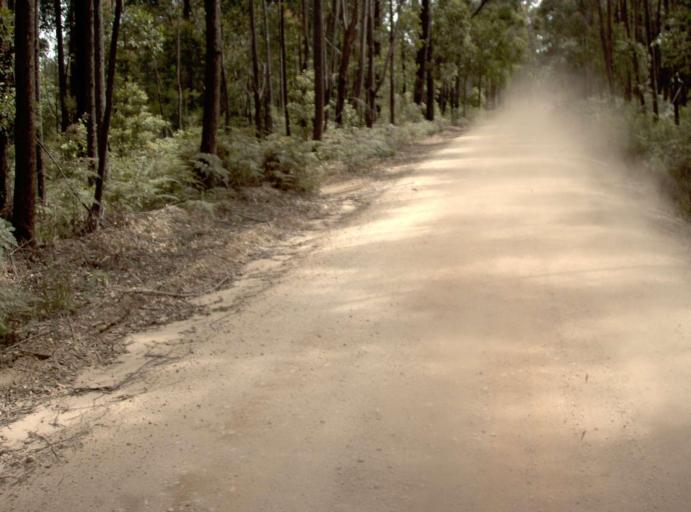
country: AU
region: Victoria
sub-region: East Gippsland
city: Lakes Entrance
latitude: -37.6210
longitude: 148.6825
